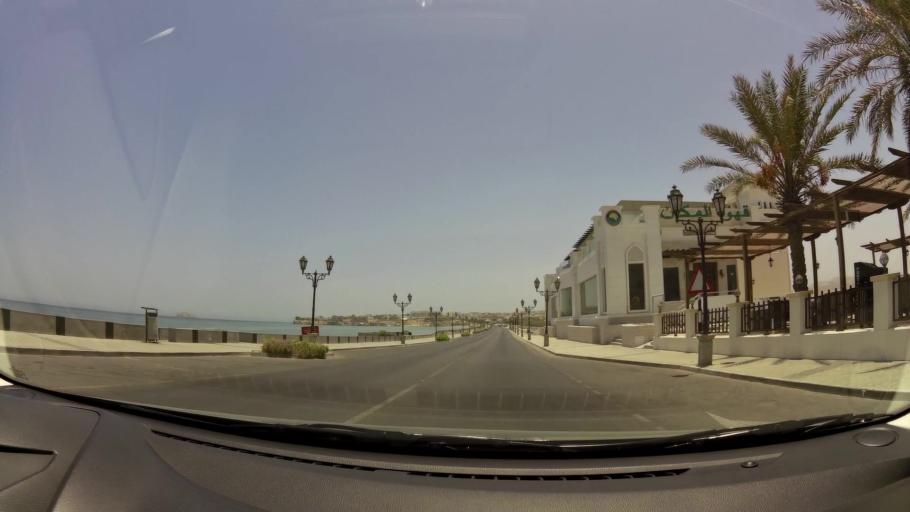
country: OM
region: Muhafazat Masqat
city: Bawshar
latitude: 23.6212
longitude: 58.4718
